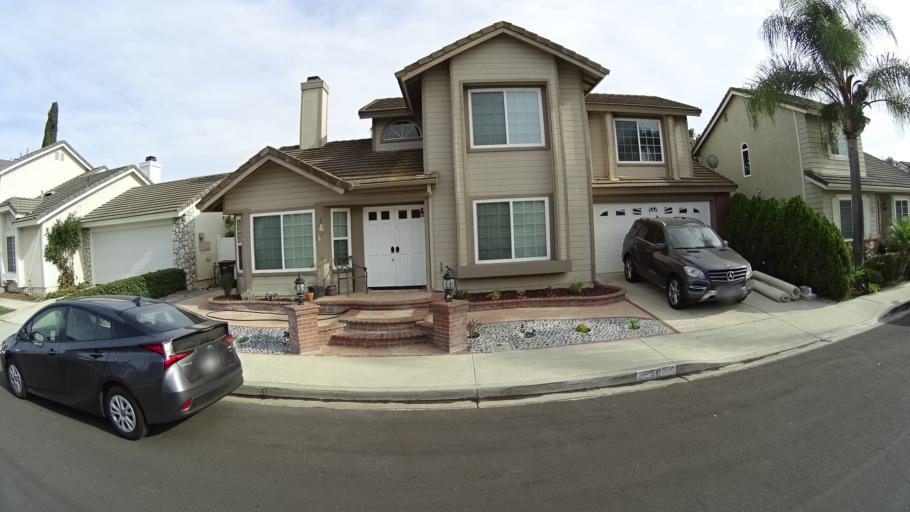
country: US
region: California
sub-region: Orange County
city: Laguna Woods
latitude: 33.5943
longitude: -117.7475
